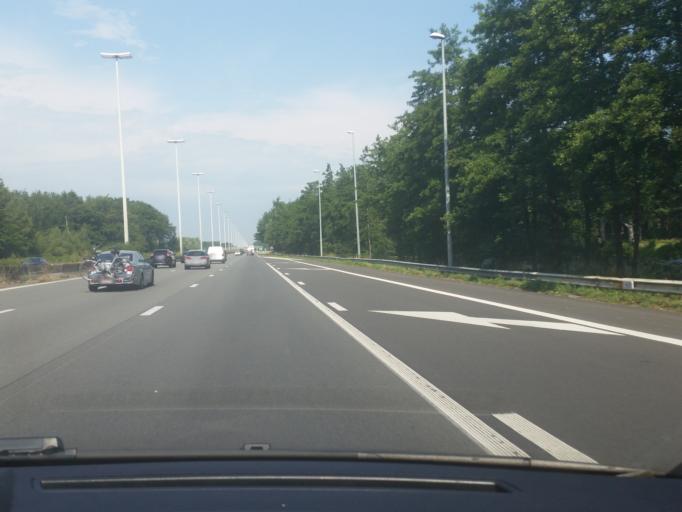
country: BE
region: Flanders
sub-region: Provincie West-Vlaanderen
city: Beernem
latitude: 51.1231
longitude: 3.3176
